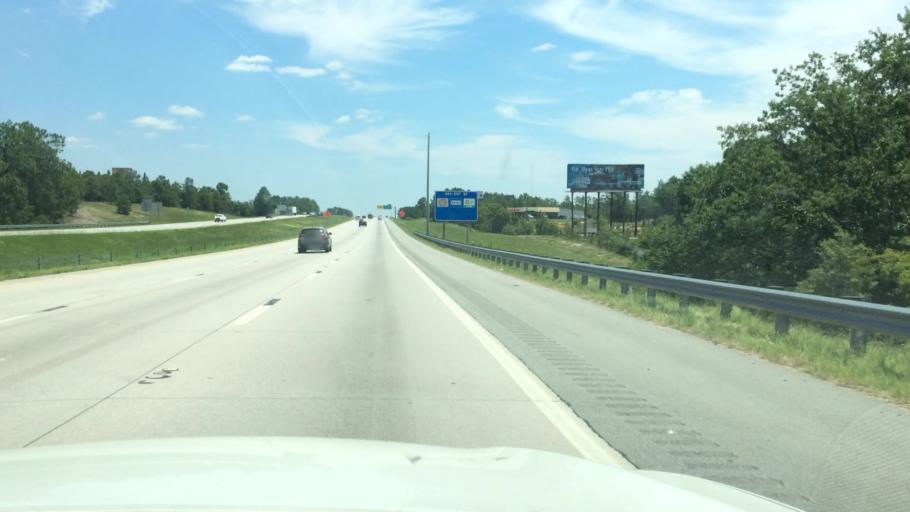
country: US
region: South Carolina
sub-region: Kershaw County
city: Elgin
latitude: 34.1008
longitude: -80.8397
